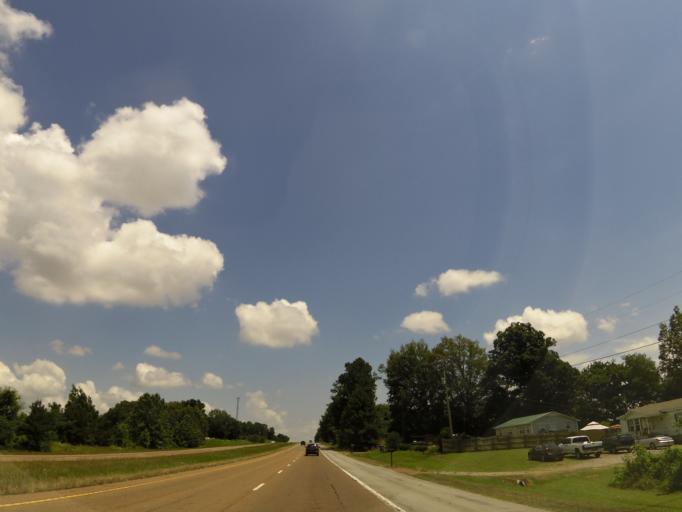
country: US
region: Tennessee
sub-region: Lauderdale County
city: Halls
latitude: 35.9142
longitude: -89.2684
